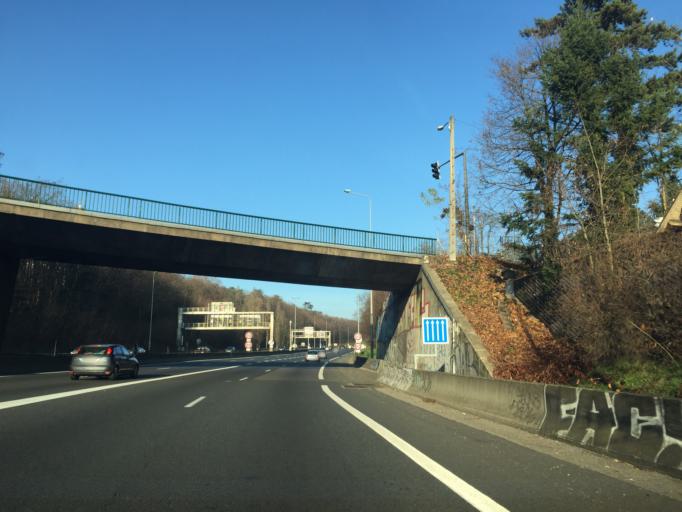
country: FR
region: Rhone-Alpes
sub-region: Departement du Rhone
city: Ecully
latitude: 45.7741
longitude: 4.7856
